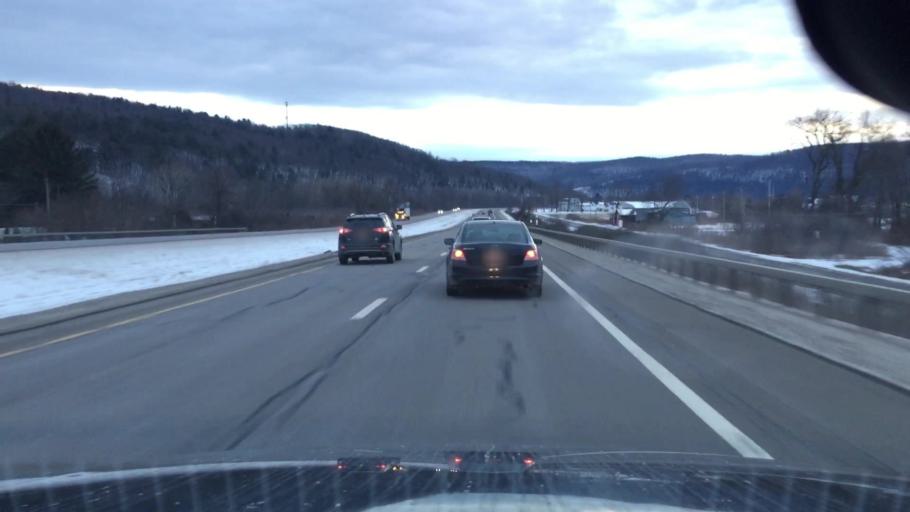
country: US
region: New York
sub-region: Steuben County
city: Gang Mills
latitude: 42.2057
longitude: -77.1688
